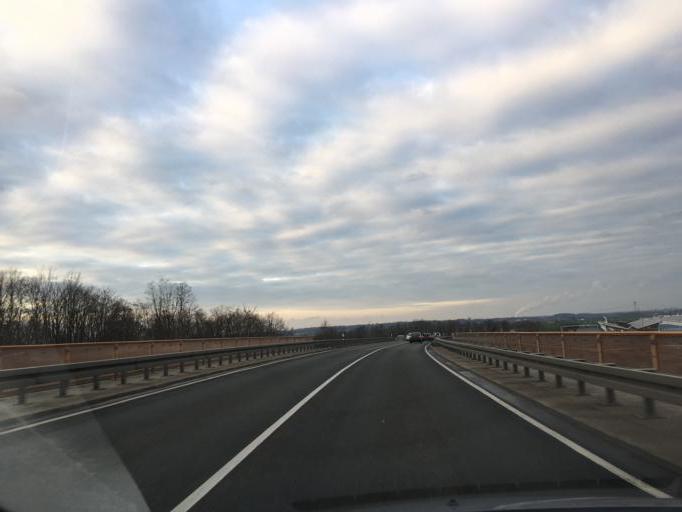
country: DE
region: Thuringia
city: Altenburg
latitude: 51.0109
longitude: 12.4556
